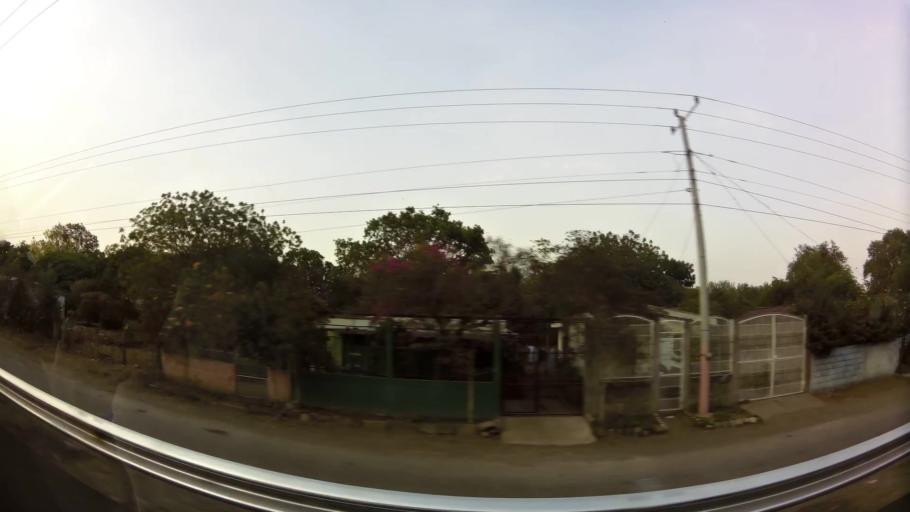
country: NI
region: Managua
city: Ciudad Sandino
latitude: 12.1851
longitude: -86.3613
